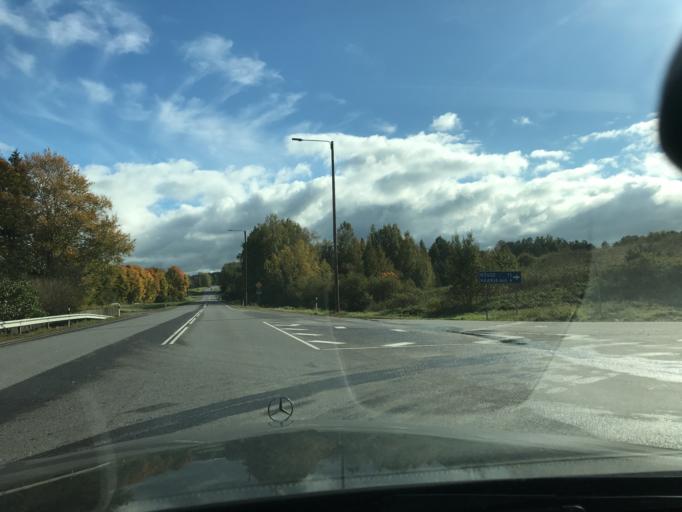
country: EE
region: Vorumaa
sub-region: Voru linn
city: Voru
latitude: 57.8090
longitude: 27.0668
